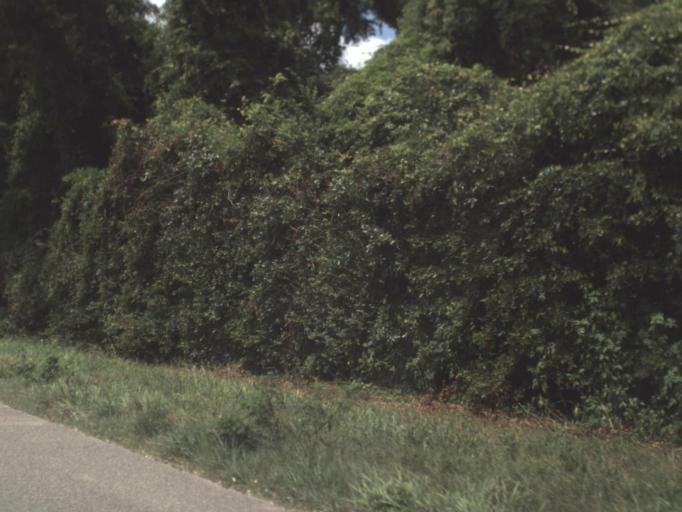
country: US
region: Florida
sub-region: Gilchrist County
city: Trenton
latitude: 29.6819
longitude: -82.8573
